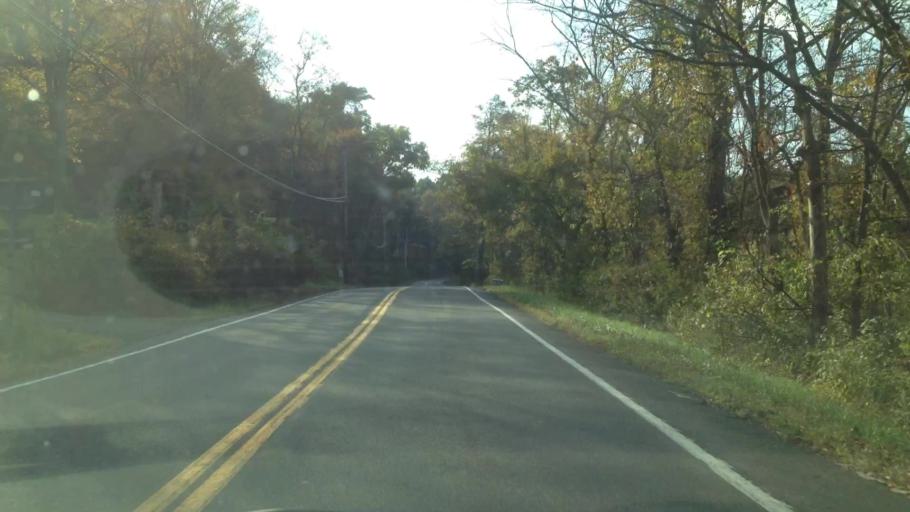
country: US
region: New York
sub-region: Ulster County
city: Tillson
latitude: 41.8263
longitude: -74.0466
